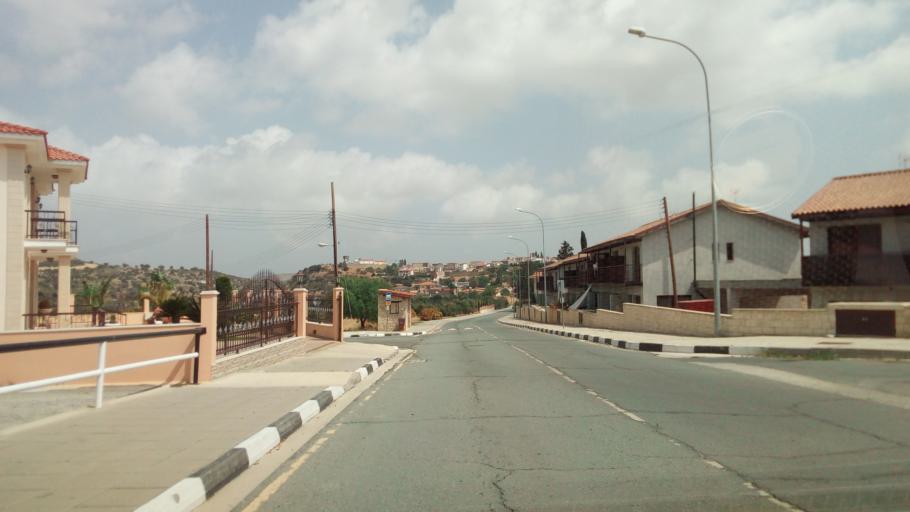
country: CY
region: Larnaka
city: Kofinou
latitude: 34.8032
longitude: 33.3278
